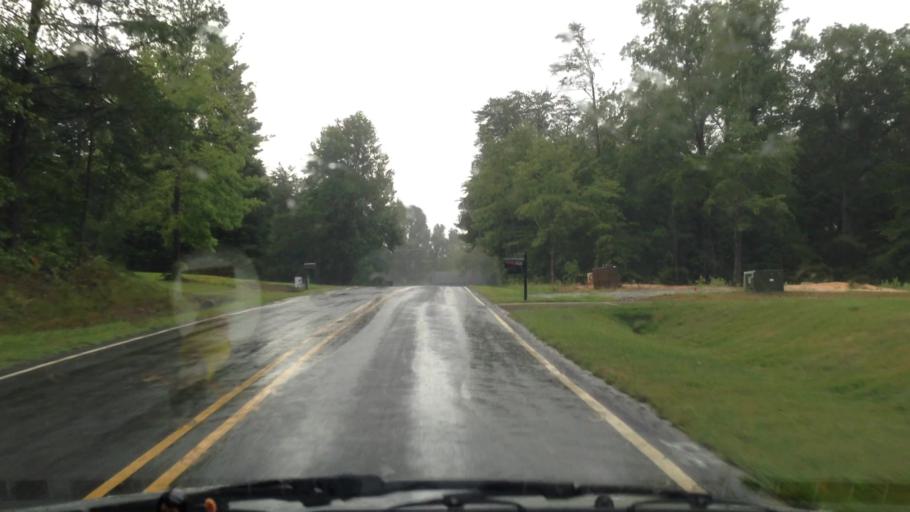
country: US
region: North Carolina
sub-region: Guilford County
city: Stokesdale
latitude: 36.2272
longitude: -80.0307
